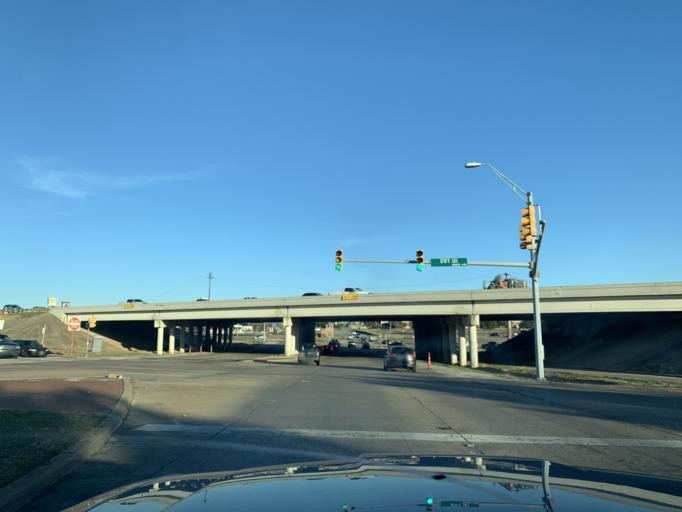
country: US
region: Texas
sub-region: Tarrant County
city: Bedford
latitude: 32.8518
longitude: -97.1118
